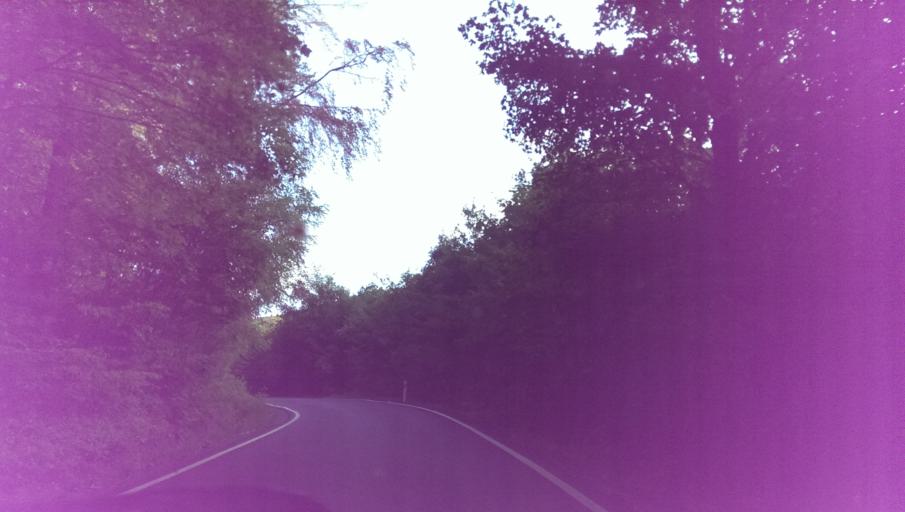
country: CZ
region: South Moravian
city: Zeravice
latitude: 49.0726
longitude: 17.2226
